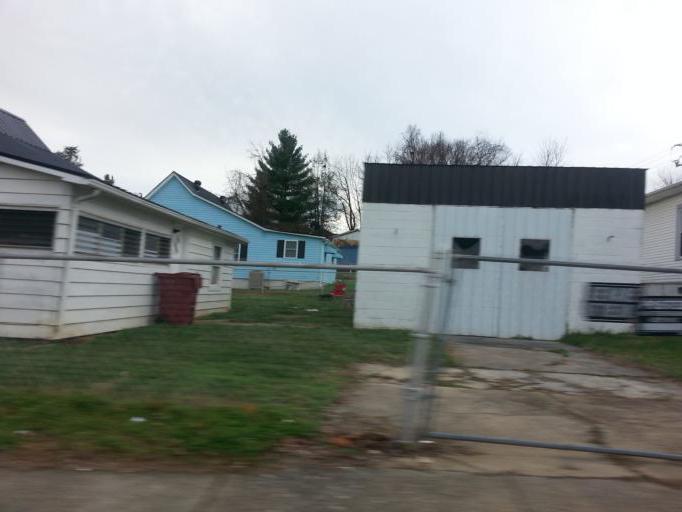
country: US
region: Tennessee
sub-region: Washington County
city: Johnson City
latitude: 36.3143
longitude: -82.3739
